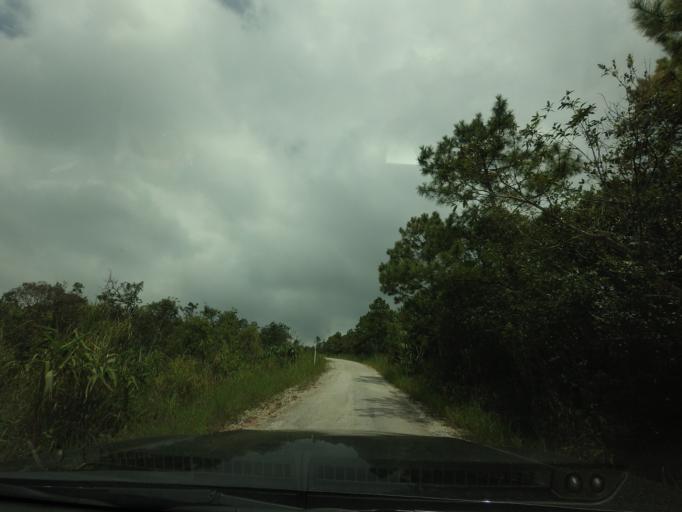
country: TH
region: Loei
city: Phu Ruea
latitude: 17.5031
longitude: 101.3413
